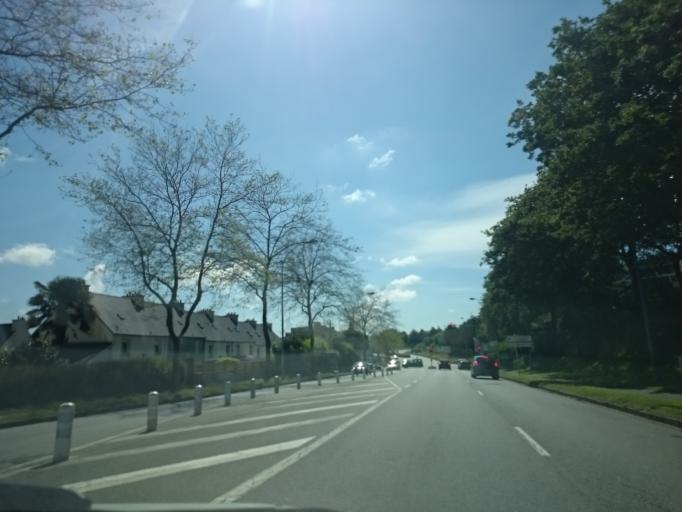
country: FR
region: Brittany
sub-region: Departement du Finistere
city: Brest
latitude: 48.4157
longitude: -4.4739
